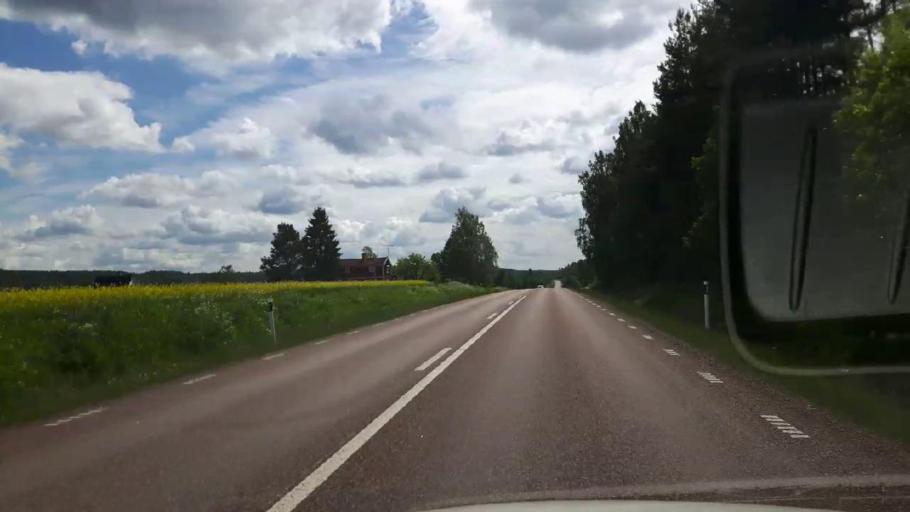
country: SE
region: Dalarna
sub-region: Hedemora Kommun
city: Hedemora
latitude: 60.3784
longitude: 15.9123
